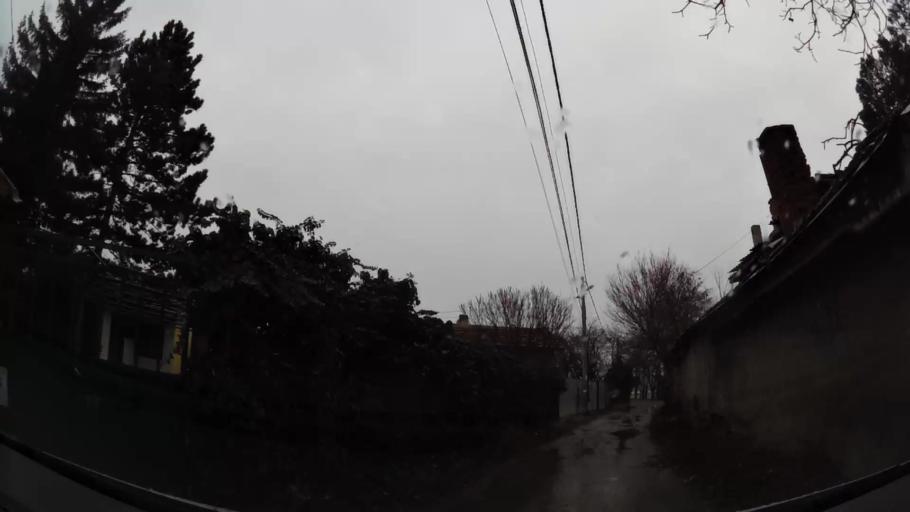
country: BG
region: Sofia-Capital
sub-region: Stolichna Obshtina
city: Sofia
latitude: 42.6573
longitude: 23.4292
